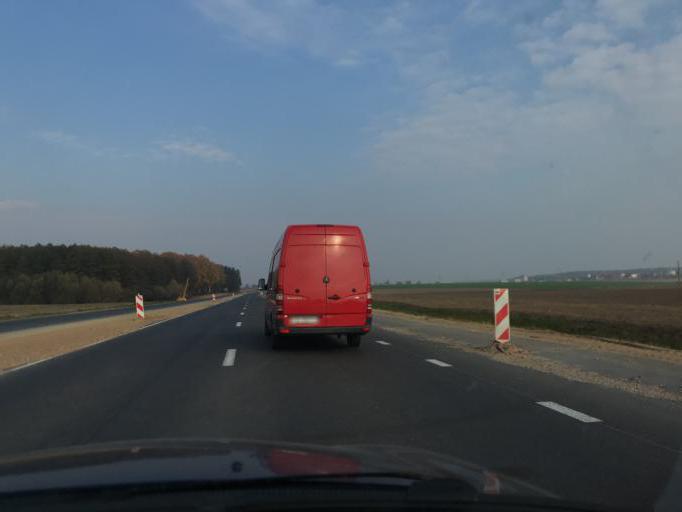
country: BY
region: Grodnenskaya
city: Shchuchin
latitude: 53.7172
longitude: 24.9570
